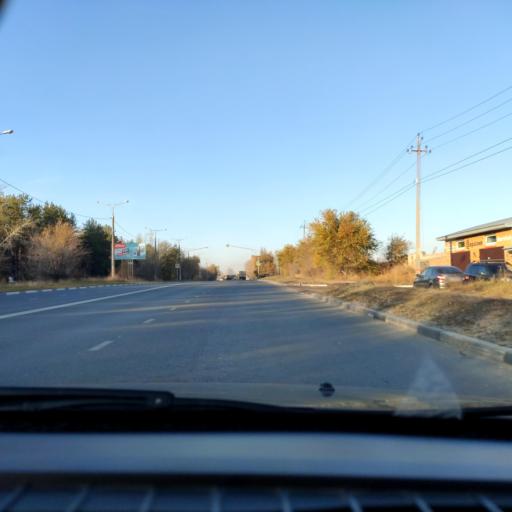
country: RU
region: Samara
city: Zhigulevsk
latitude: 53.4888
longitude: 49.4743
